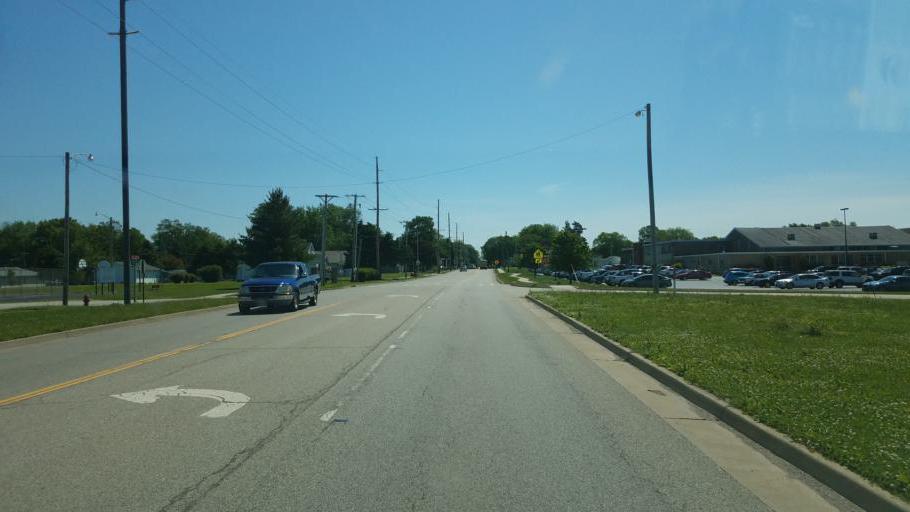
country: US
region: Illinois
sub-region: McLean County
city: Heyworth
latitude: 40.3120
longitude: -88.9835
